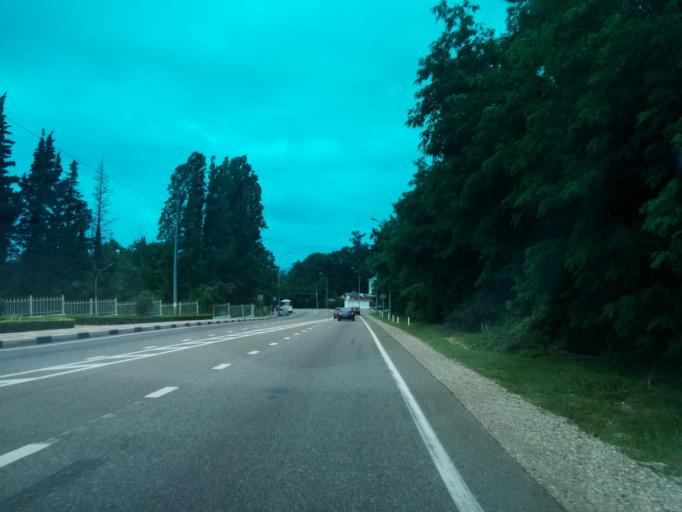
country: RU
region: Krasnodarskiy
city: Nebug
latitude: 44.1773
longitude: 38.9484
